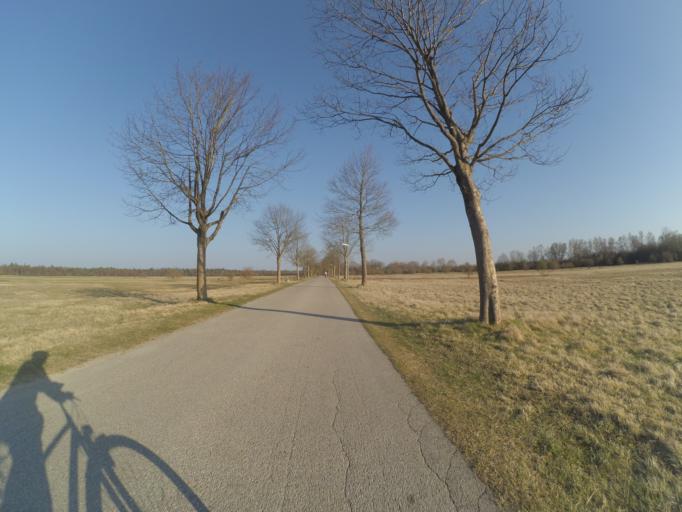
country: DE
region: Bavaria
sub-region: Upper Bavaria
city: Oberschleissheim
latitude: 48.2396
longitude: 11.5715
